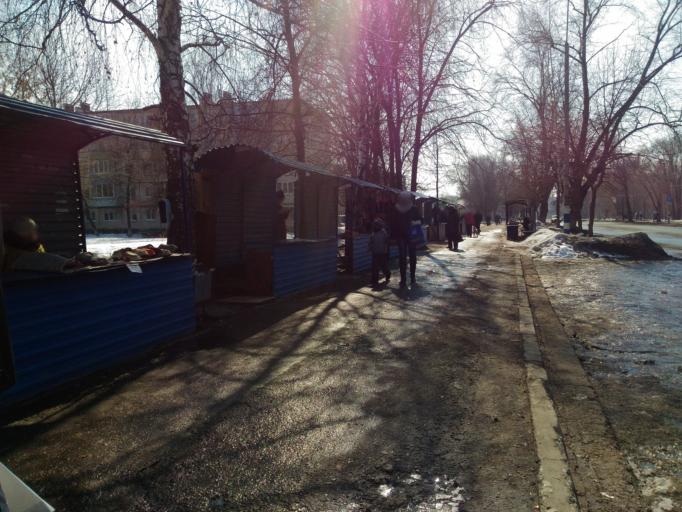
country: RU
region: Ulyanovsk
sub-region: Ulyanovskiy Rayon
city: Ulyanovsk
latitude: 54.3297
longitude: 48.4838
